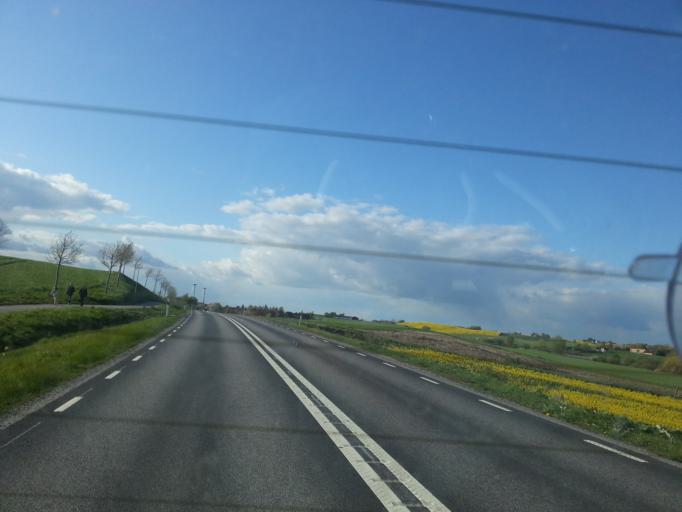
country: SE
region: Skane
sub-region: Ystads Kommun
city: Ystad
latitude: 55.4464
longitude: 13.8049
